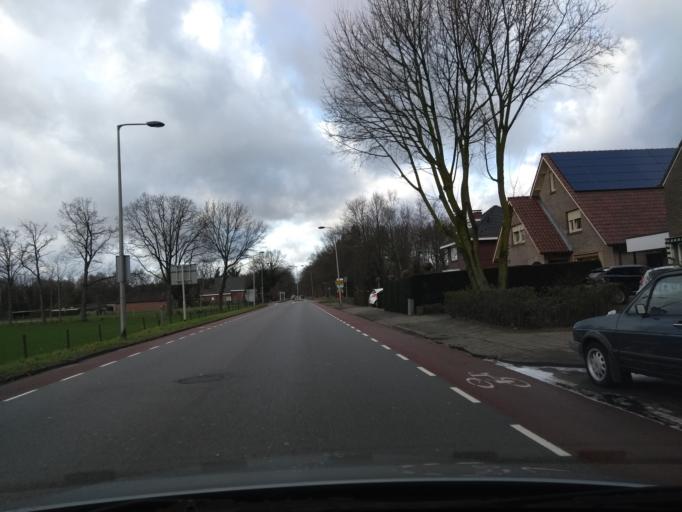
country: NL
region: Overijssel
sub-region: Gemeente Enschede
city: Enschede
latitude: 52.2420
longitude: 6.8827
